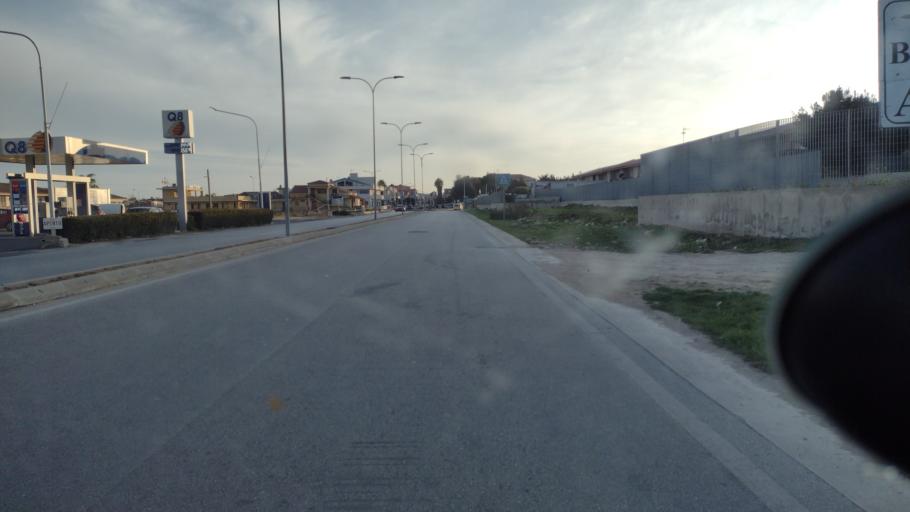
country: IT
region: Sicily
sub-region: Provincia di Siracusa
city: Avola
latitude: 36.9180
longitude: 15.1455
